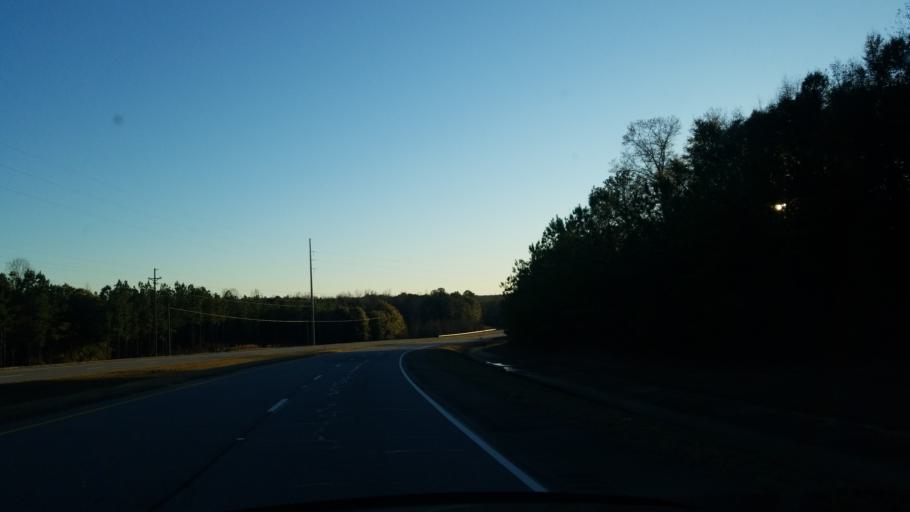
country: US
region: Georgia
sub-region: Chattahoochee County
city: Cusseta
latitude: 32.2745
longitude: -84.7816
